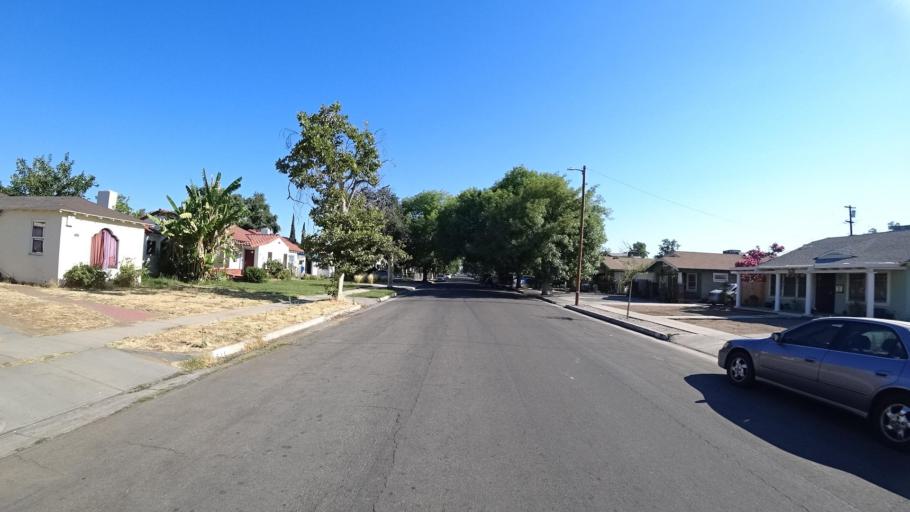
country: US
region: California
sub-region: Fresno County
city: Fresno
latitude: 36.7526
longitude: -119.8130
